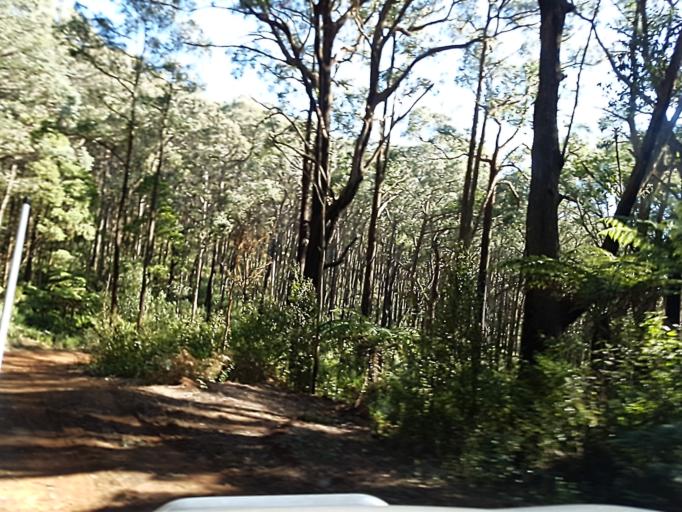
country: AU
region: Victoria
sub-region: Yarra Ranges
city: Healesville
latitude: -37.5669
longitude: 145.4989
